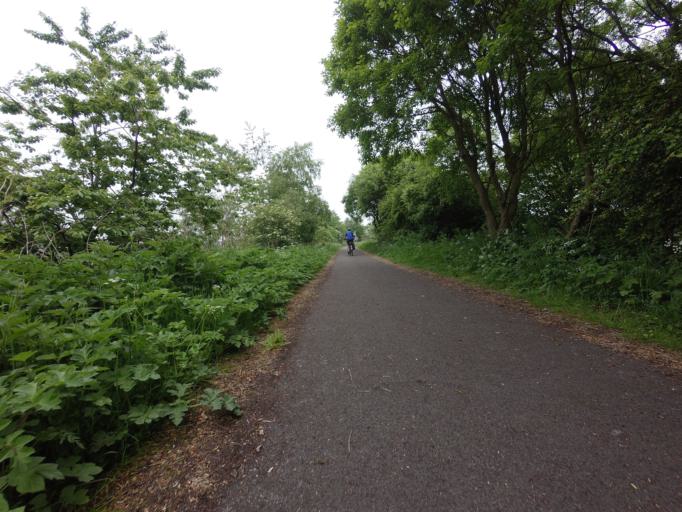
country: GB
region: Scotland
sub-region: Fife
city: Townhill
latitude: 56.0925
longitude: -3.4443
